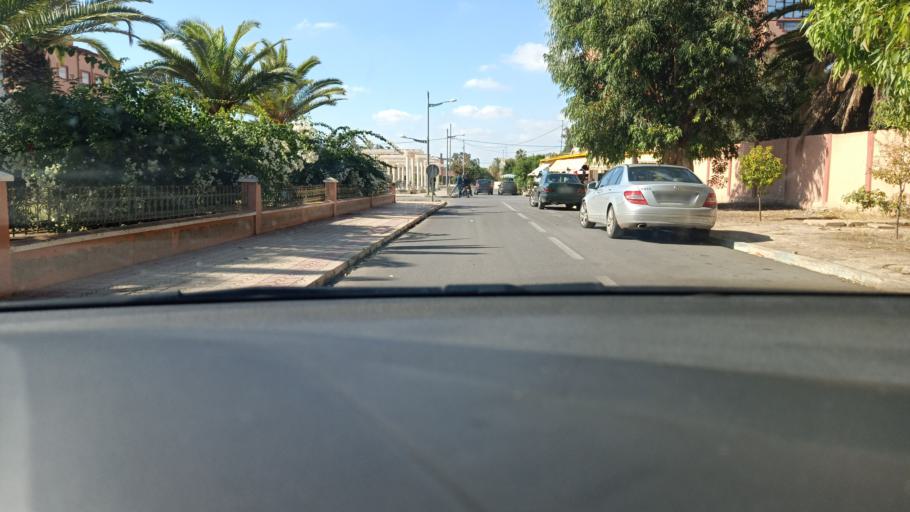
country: MA
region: Doukkala-Abda
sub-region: Safi
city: Youssoufia
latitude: 32.2465
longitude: -8.5322
